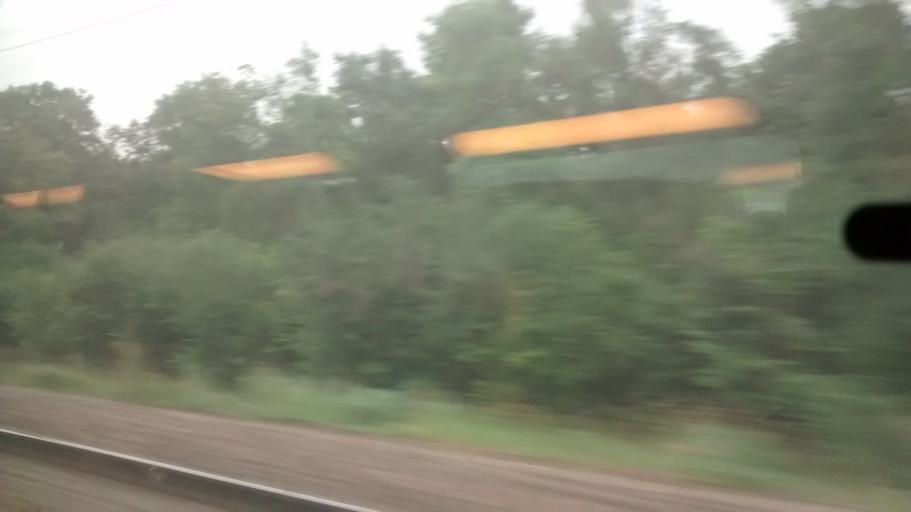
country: FR
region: Ile-de-France
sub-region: Departement de Seine-et-Marne
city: Saint-Germain-Laval
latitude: 48.3864
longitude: 2.9925
